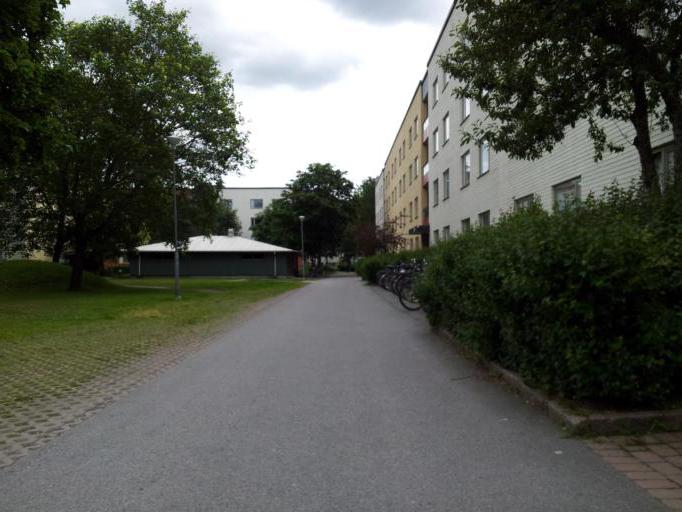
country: SE
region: Uppsala
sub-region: Uppsala Kommun
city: Uppsala
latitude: 59.8734
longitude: 17.6436
